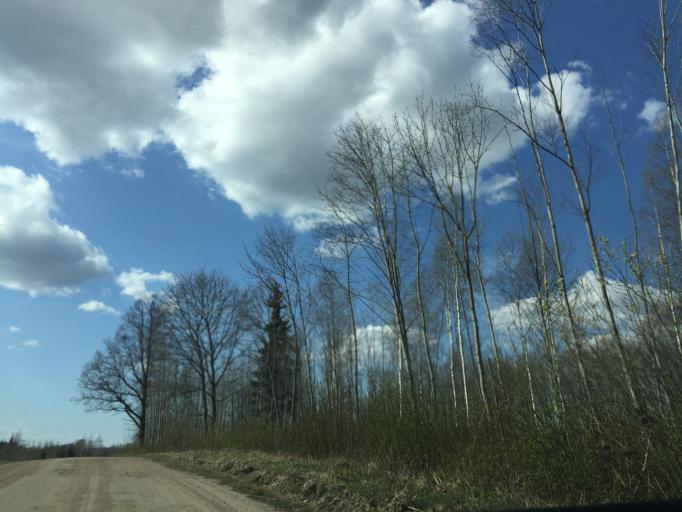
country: LV
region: Skriveri
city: Skriveri
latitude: 56.7928
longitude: 25.1581
